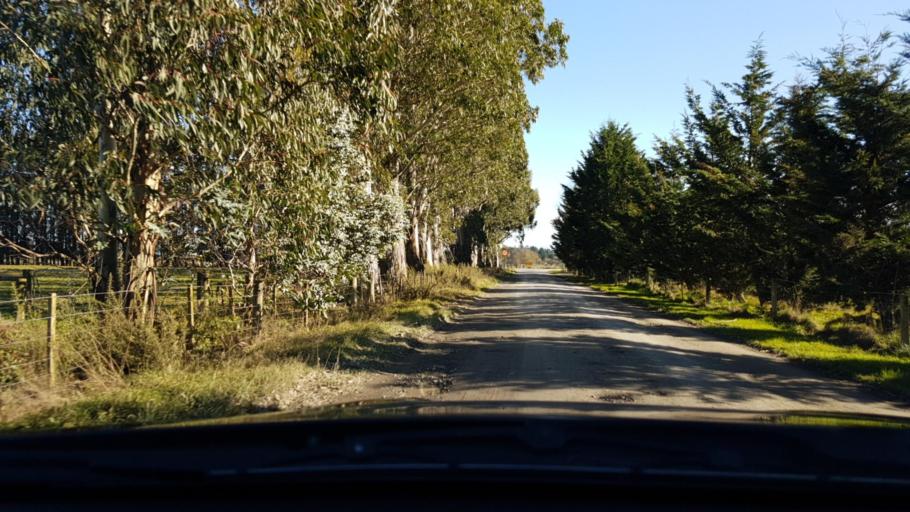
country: NZ
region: Canterbury
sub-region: Waimakariri District
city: Oxford
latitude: -43.2926
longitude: 172.1761
